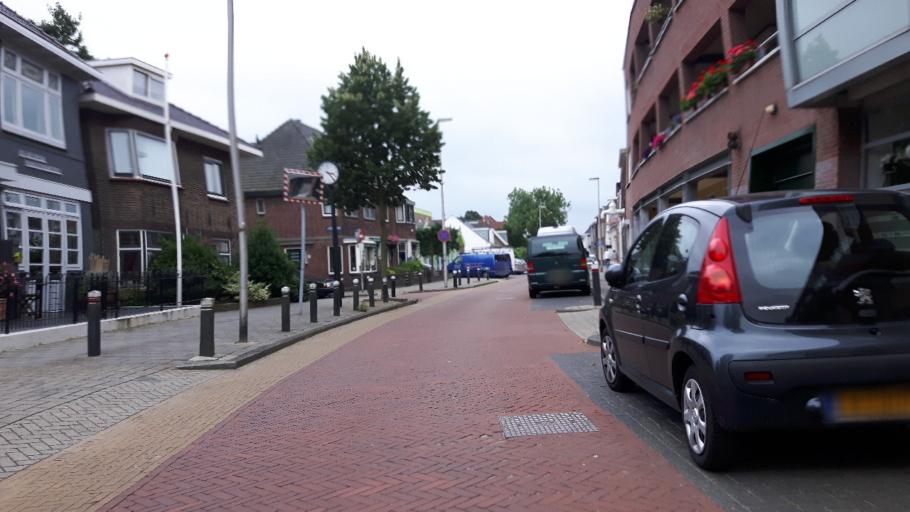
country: NL
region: South Holland
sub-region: Gemeente Alphen aan den Rijn
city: Alphen aan den Rijn
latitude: 52.1377
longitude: 4.6636
